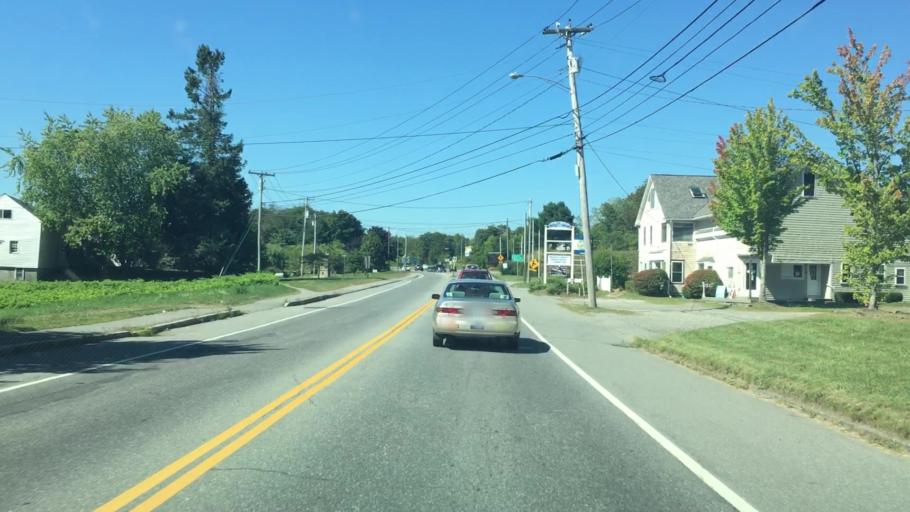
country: US
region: Maine
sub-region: Waldo County
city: Belfast
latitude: 44.4341
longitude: -69.0020
